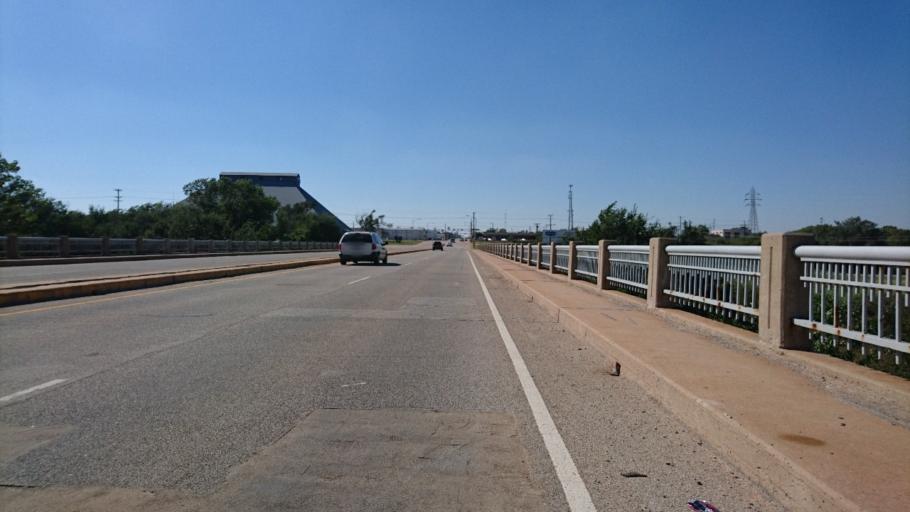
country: US
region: Oklahoma
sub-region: Custer County
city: Clinton
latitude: 35.5156
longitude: -98.9568
